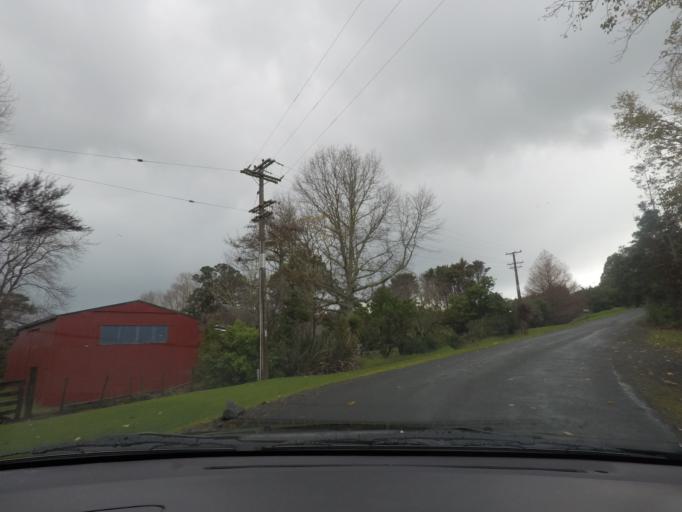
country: NZ
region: Auckland
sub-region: Auckland
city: Warkworth
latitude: -36.4726
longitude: 174.7360
